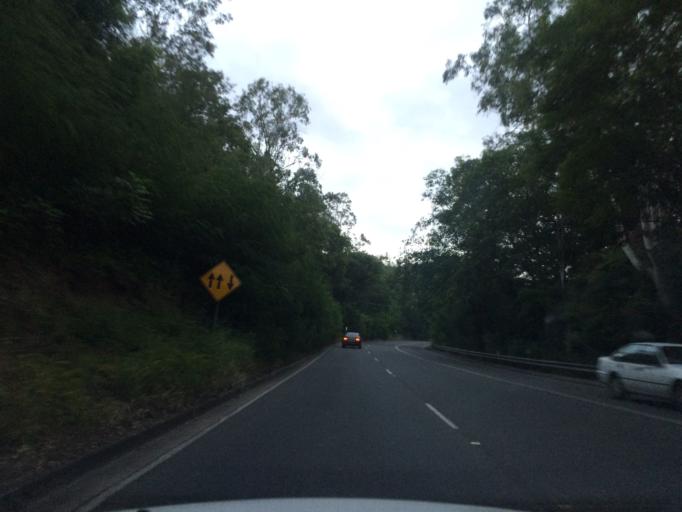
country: AU
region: Queensland
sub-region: Brisbane
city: Kenmore Hills
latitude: -27.5138
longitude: 152.9331
